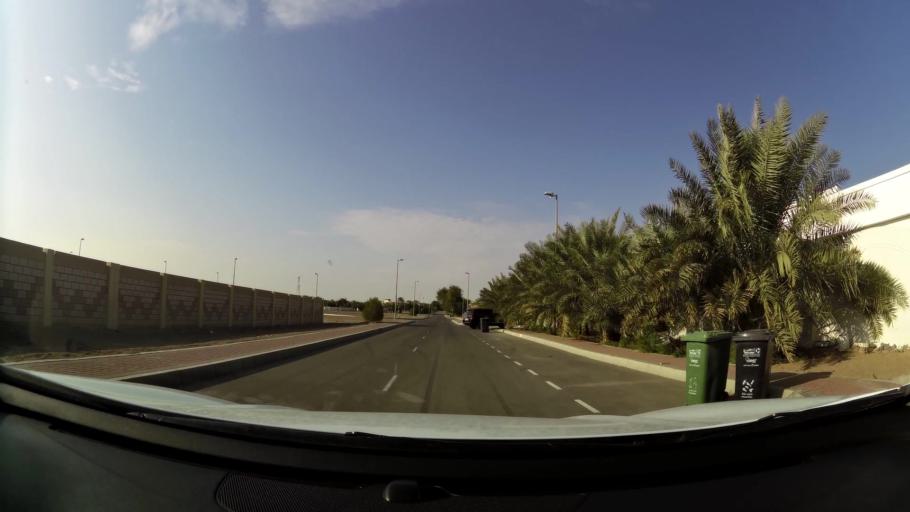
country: AE
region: Abu Dhabi
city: Al Ain
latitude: 24.0765
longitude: 55.8420
